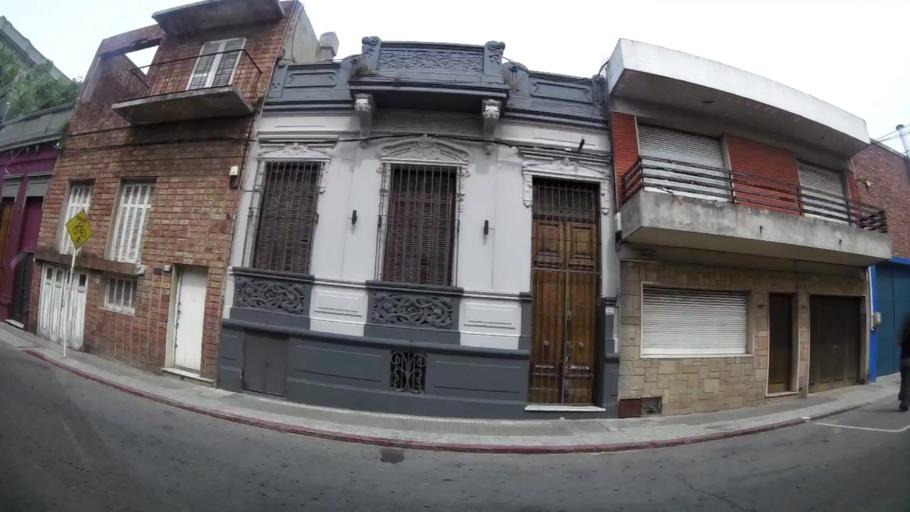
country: UY
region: Montevideo
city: Montevideo
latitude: -34.9112
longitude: -56.1781
